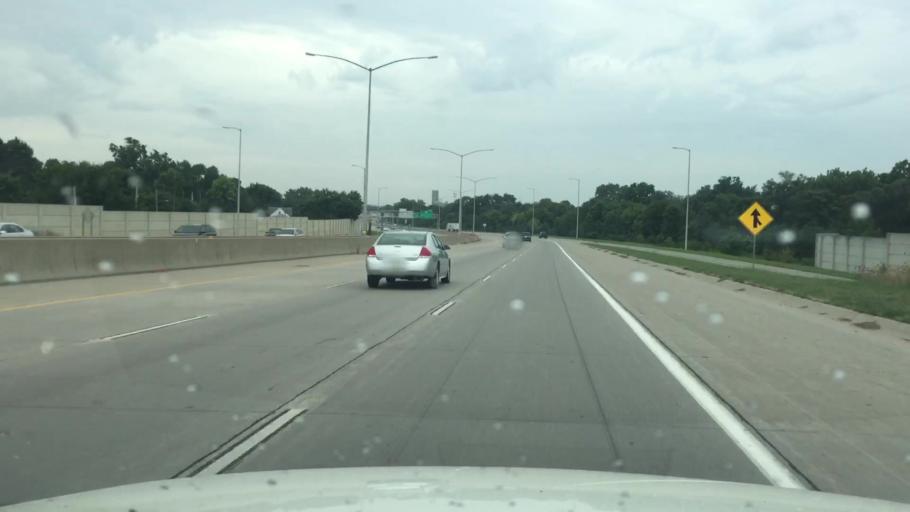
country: US
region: Iowa
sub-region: Polk County
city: Des Moines
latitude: 41.6139
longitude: -93.5781
